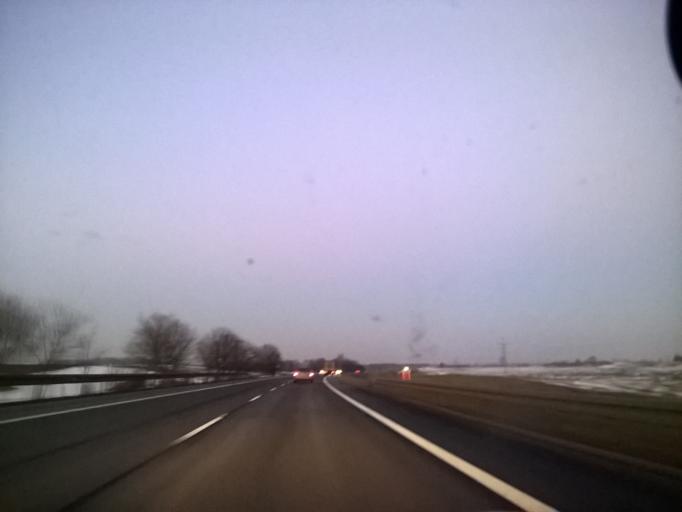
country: PL
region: Warmian-Masurian Voivodeship
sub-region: Powiat olsztynski
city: Biskupiec
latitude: 53.8387
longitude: 20.9309
